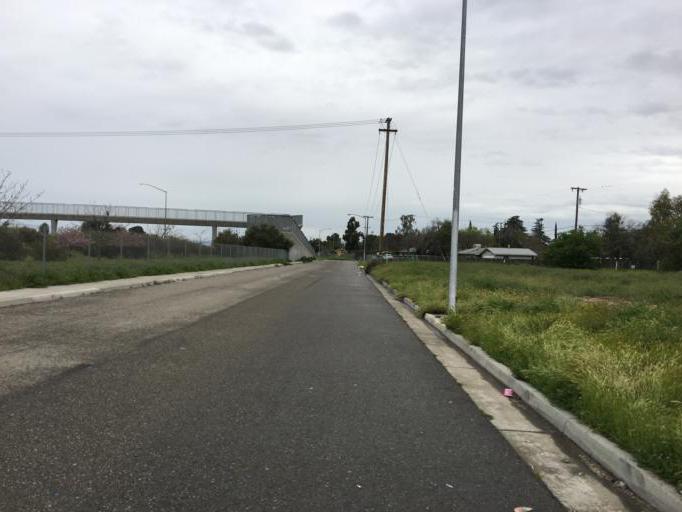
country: US
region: California
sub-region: Fresno County
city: Sunnyside
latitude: 36.7535
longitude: -119.7336
